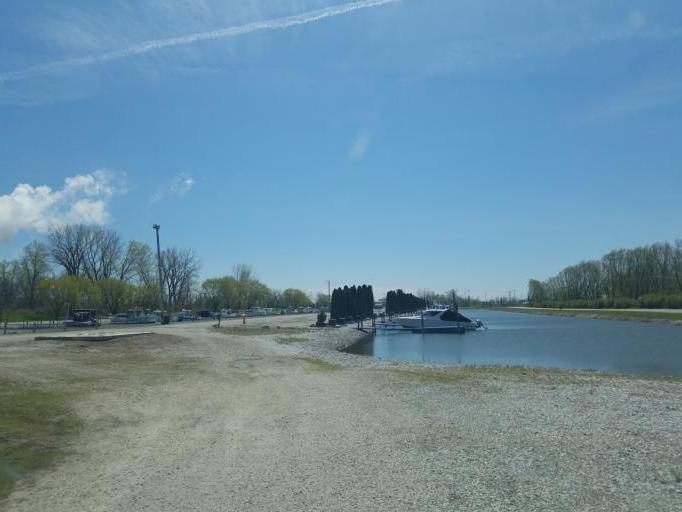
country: US
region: Ohio
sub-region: Ottawa County
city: Oak Harbor
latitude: 41.6077
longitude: -83.1066
